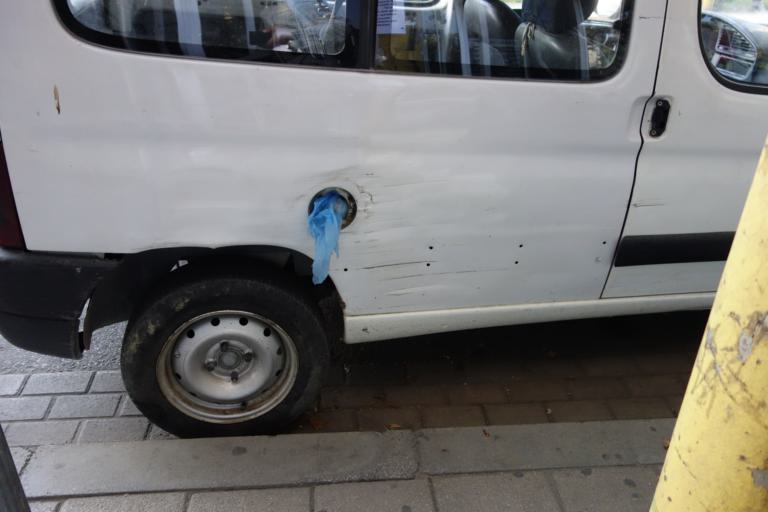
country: AL
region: Tirane
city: Tirana
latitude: 41.3231
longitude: 19.8154
